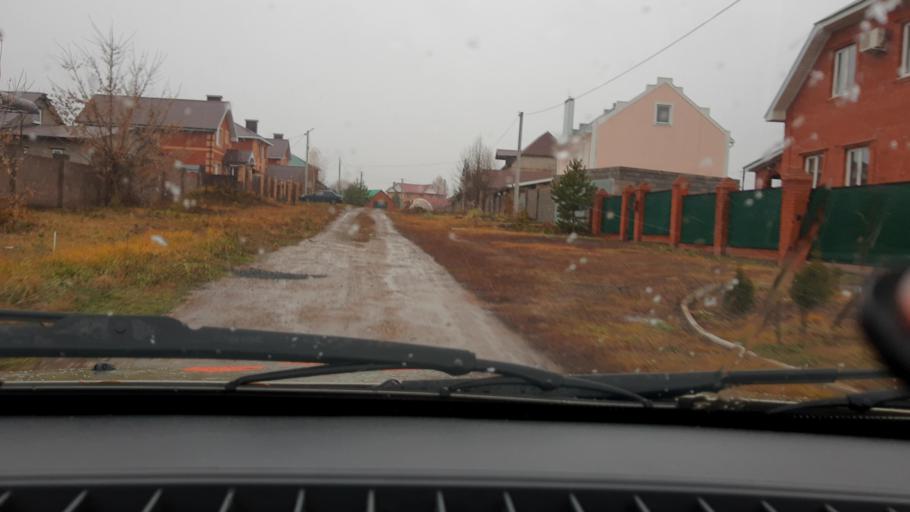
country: RU
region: Bashkortostan
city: Ufa
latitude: 54.6119
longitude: 55.9182
